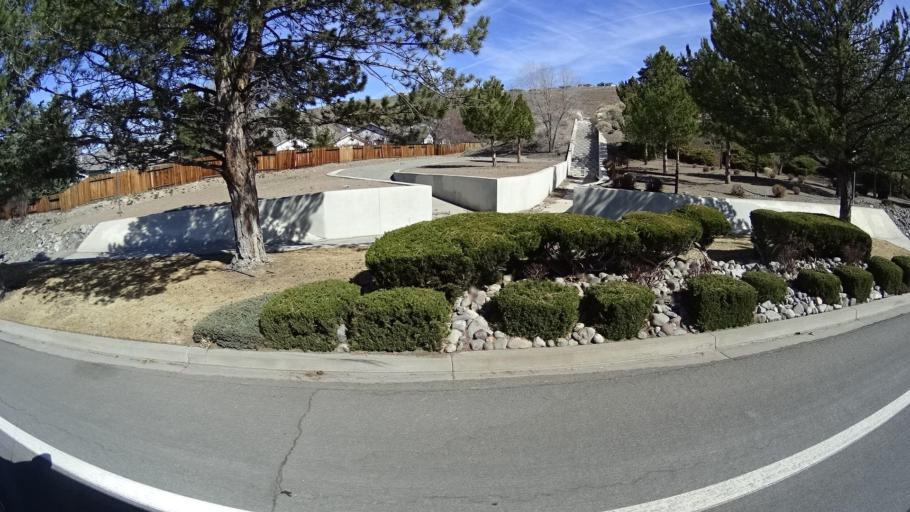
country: US
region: Nevada
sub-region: Washoe County
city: Spanish Springs
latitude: 39.5848
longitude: -119.7073
